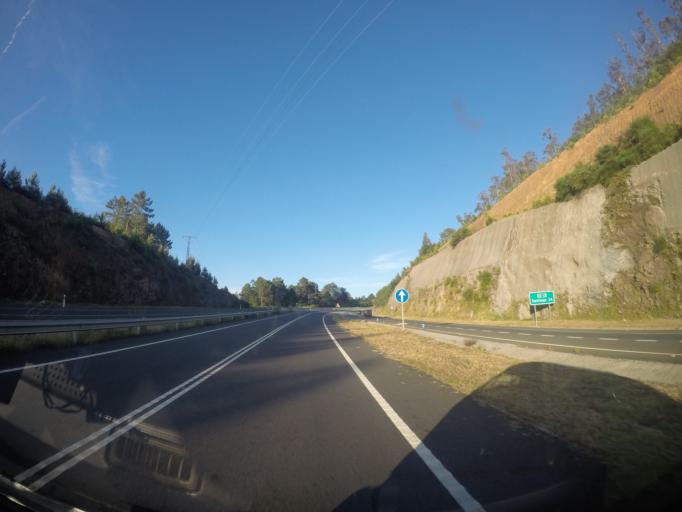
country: ES
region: Galicia
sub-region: Provincia da Coruna
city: Noia
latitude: 42.8116
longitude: -8.8750
